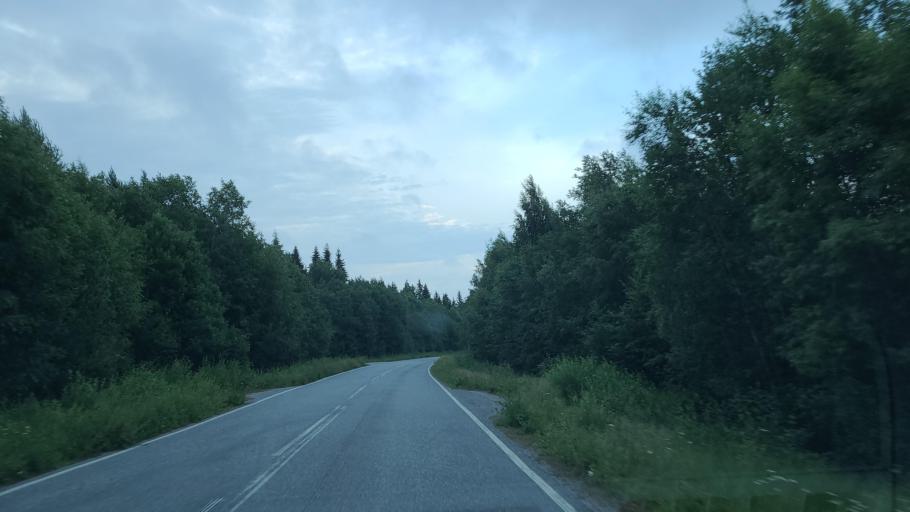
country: FI
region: Ostrobothnia
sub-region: Vaasa
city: Replot
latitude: 63.2730
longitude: 21.1573
